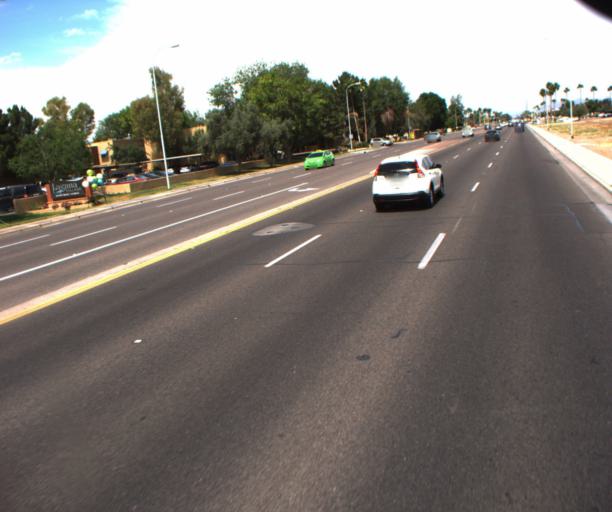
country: US
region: Arizona
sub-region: Maricopa County
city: San Carlos
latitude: 33.3441
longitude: -111.8417
